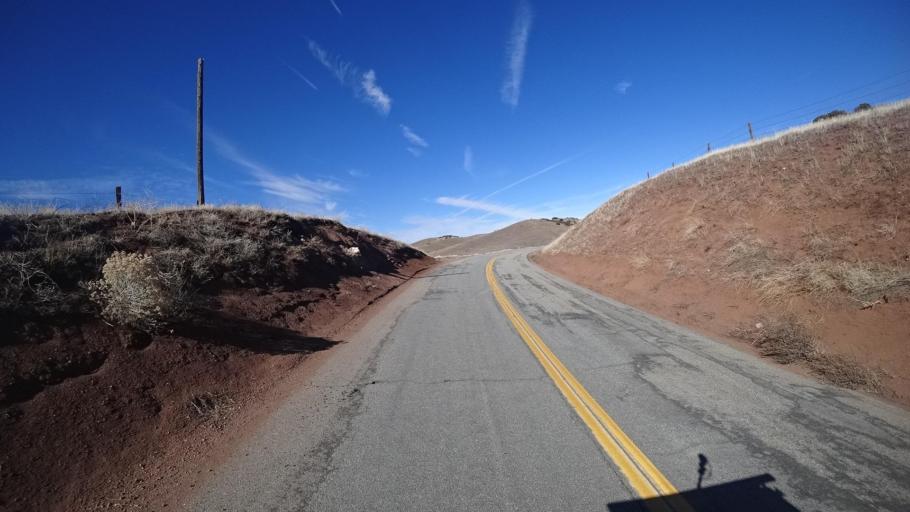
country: US
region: California
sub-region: Kern County
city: Maricopa
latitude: 34.8876
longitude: -119.3559
